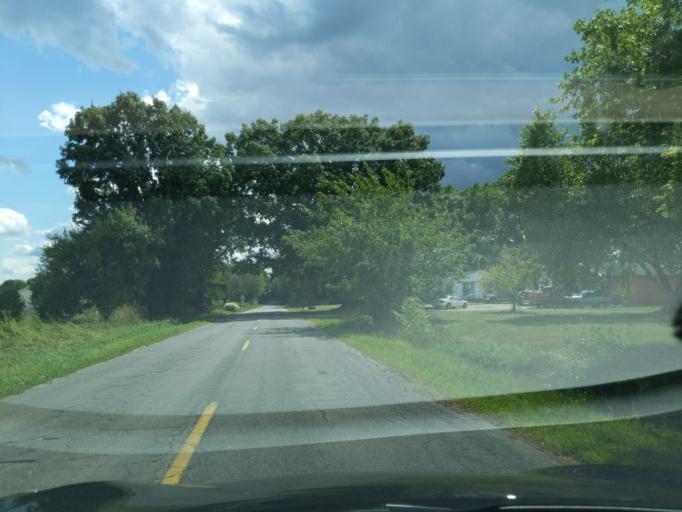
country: US
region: Michigan
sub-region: Eaton County
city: Eaton Rapids
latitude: 42.4652
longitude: -84.5805
